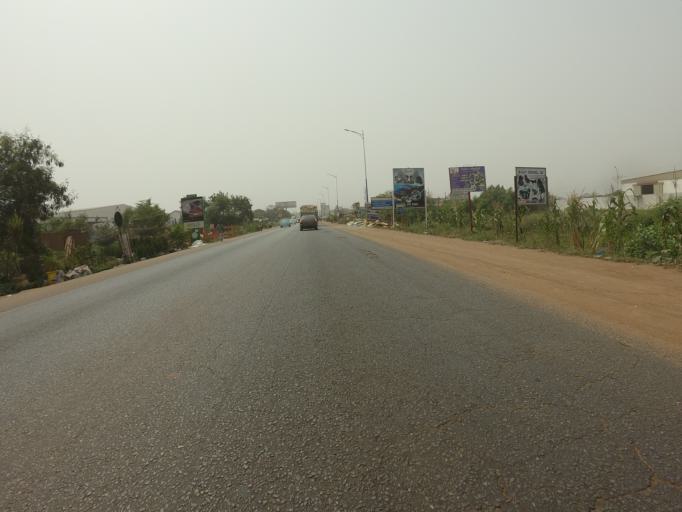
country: GH
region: Greater Accra
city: Tema
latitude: 5.7195
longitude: 0.0175
